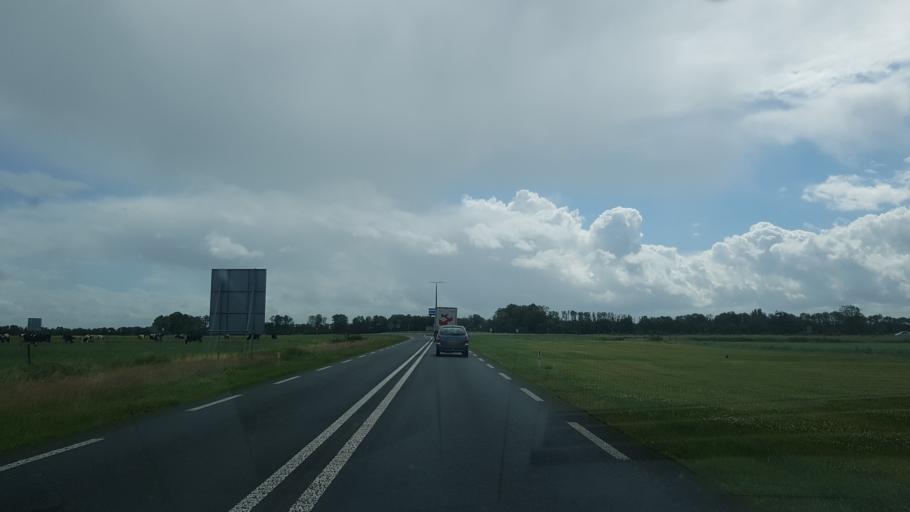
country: NL
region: Friesland
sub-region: Gemeente Dantumadiel
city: Walterswald
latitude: 53.3110
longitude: 6.0172
